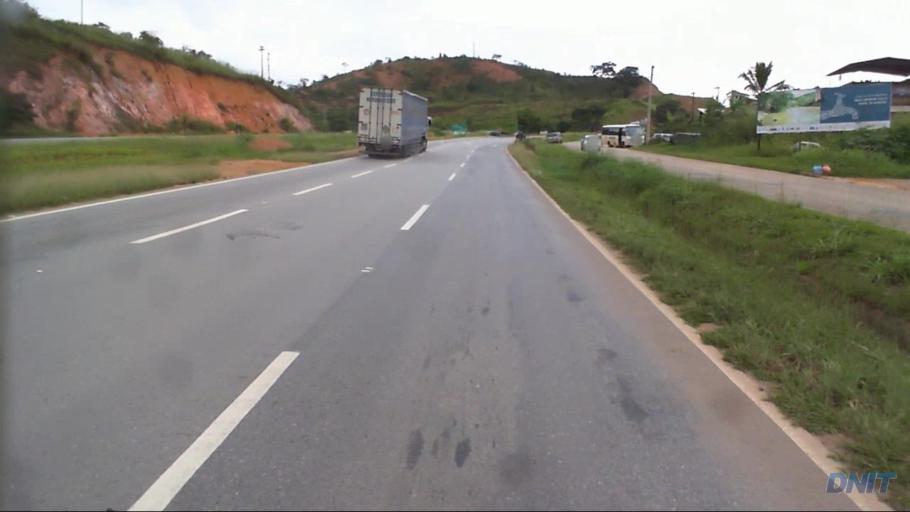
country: BR
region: Minas Gerais
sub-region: Nova Era
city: Nova Era
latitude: -19.7550
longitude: -43.0273
